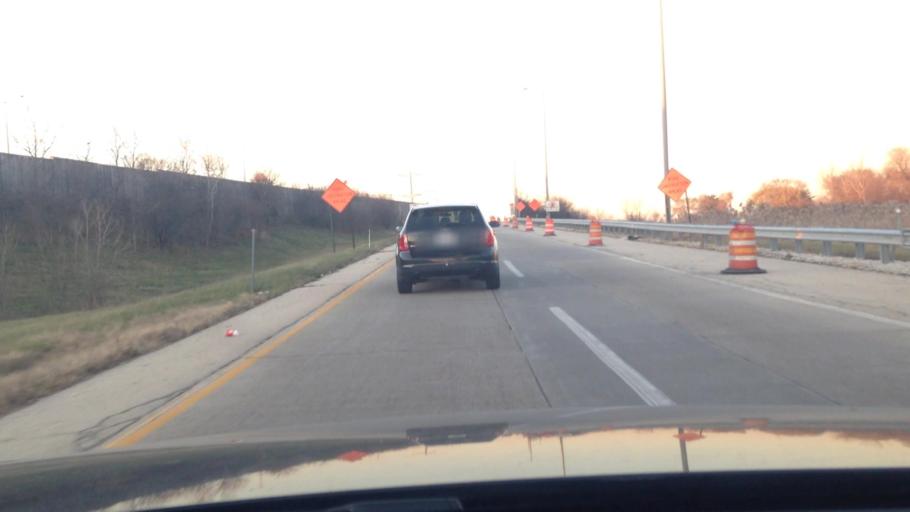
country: US
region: Illinois
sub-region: DuPage County
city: Glen Ellyn
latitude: 41.8602
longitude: -88.0406
